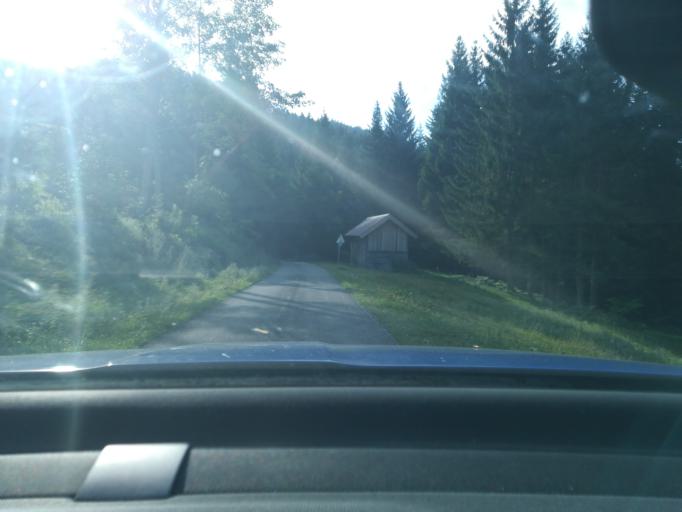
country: AT
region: Salzburg
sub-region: Politischer Bezirk Hallein
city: Abtenau
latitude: 47.5637
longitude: 13.4110
